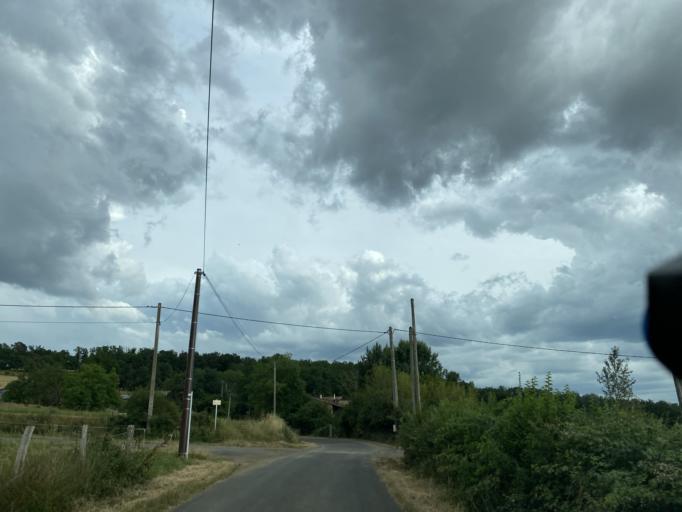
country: FR
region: Auvergne
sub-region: Departement du Puy-de-Dome
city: Peschadoires
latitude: 45.7604
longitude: 3.4514
